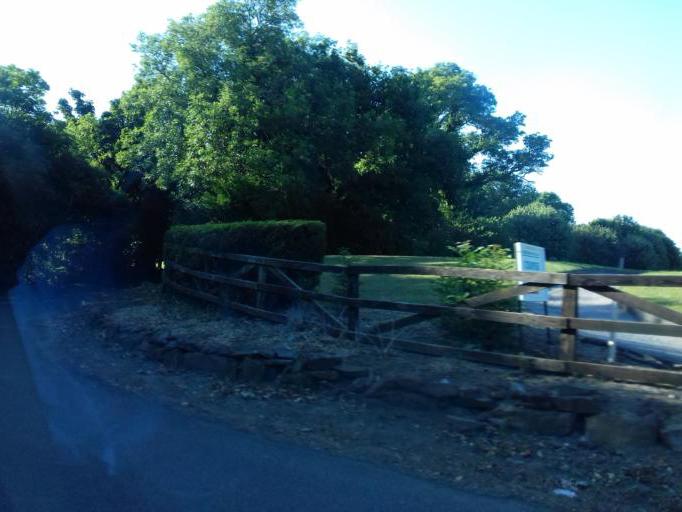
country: IE
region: Leinster
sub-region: Dublin City
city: Finglas
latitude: 53.4592
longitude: -6.3242
